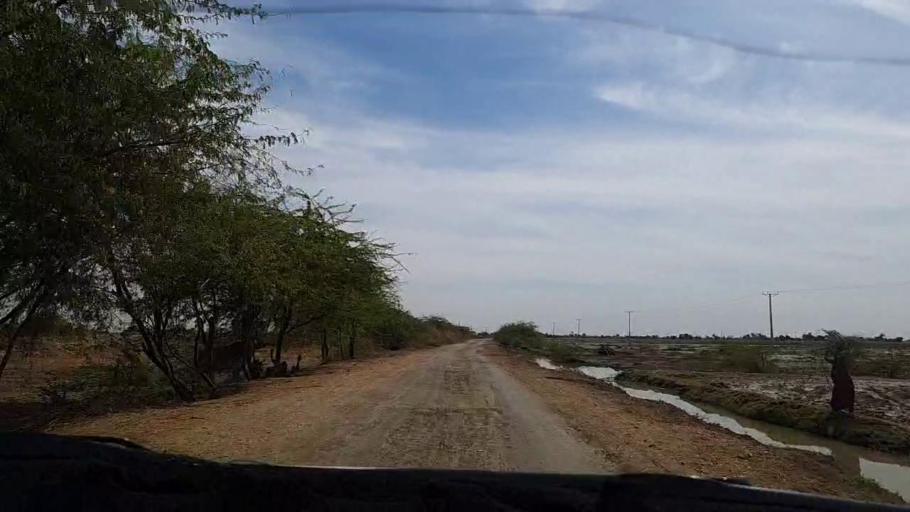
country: PK
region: Sindh
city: Pithoro
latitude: 25.4570
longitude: 69.4573
